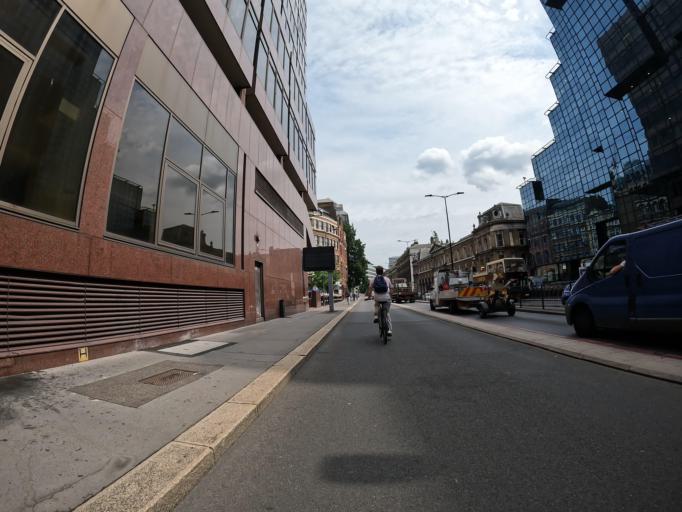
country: GB
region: England
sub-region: Greater London
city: Blackheath
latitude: 51.4860
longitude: -0.0071
